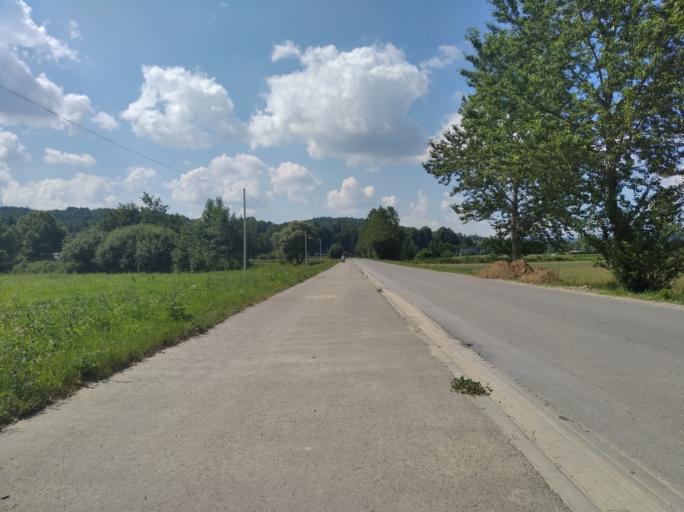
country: PL
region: Subcarpathian Voivodeship
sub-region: Powiat rzeszowski
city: Dynow
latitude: 49.7877
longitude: 22.2391
